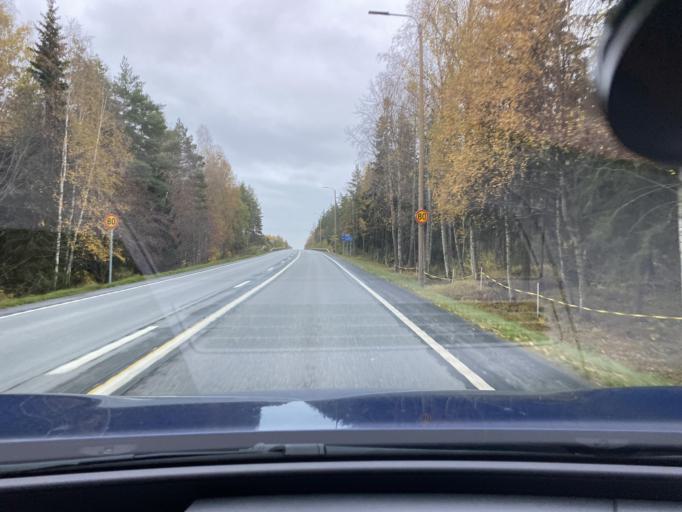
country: FI
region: Varsinais-Suomi
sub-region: Vakka-Suomi
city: Laitila
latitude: 60.9327
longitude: 21.6071
